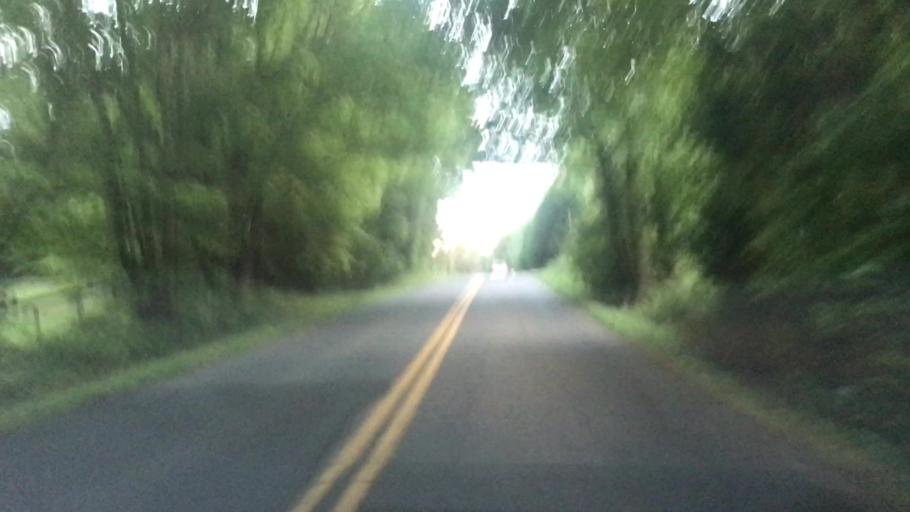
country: US
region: Virginia
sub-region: Prince William County
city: Nokesville
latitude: 38.6989
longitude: -77.6668
